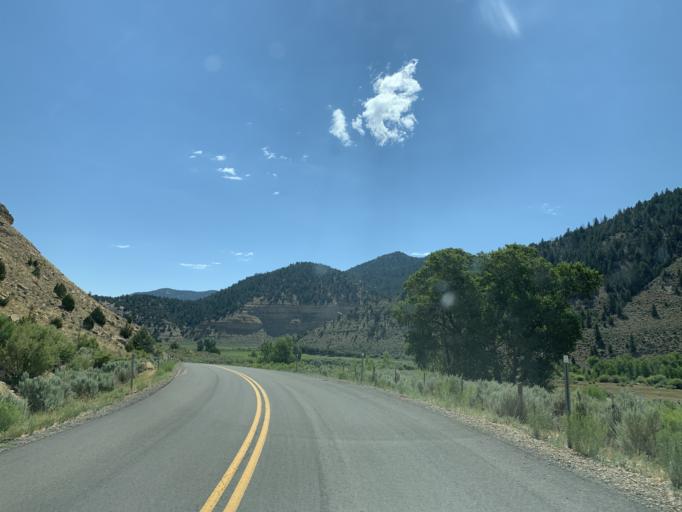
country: US
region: Utah
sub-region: Carbon County
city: East Carbon City
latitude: 39.7745
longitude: -110.4608
